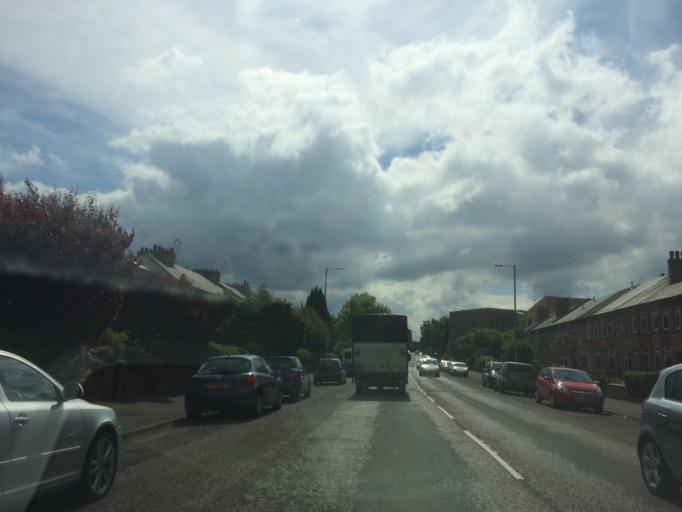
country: GB
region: Scotland
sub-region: East Renfrewshire
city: Giffnock
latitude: 55.8184
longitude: -4.2944
